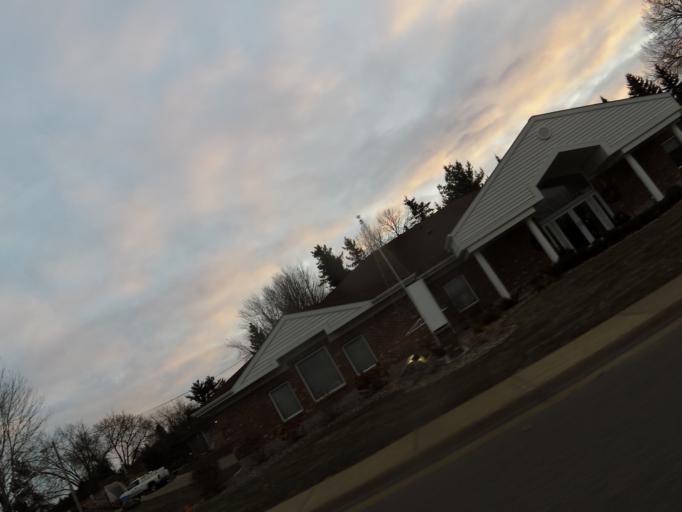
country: US
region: Minnesota
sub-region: Washington County
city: Birchwood
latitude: 45.0501
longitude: -92.9961
